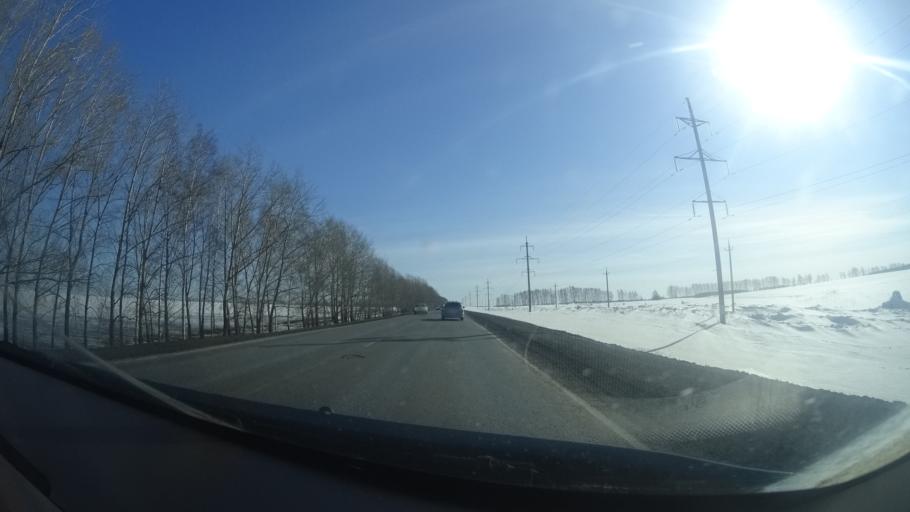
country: RU
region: Bashkortostan
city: Mikhaylovka
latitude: 54.8591
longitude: 55.7587
